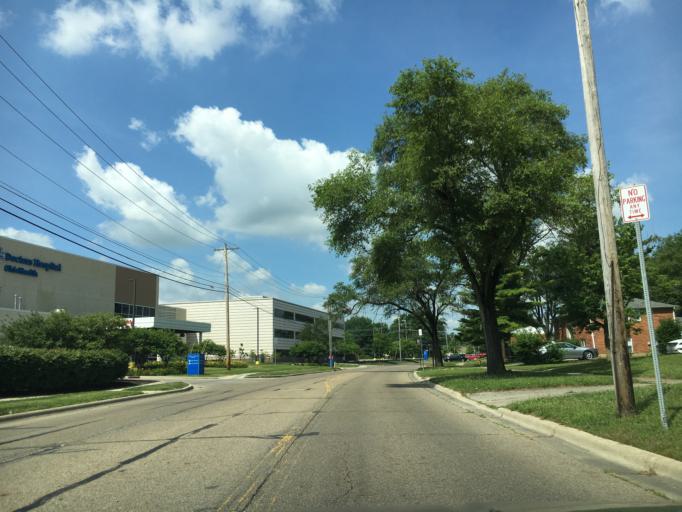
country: US
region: Ohio
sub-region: Franklin County
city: Lincoln Village
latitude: 39.9543
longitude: -83.1368
